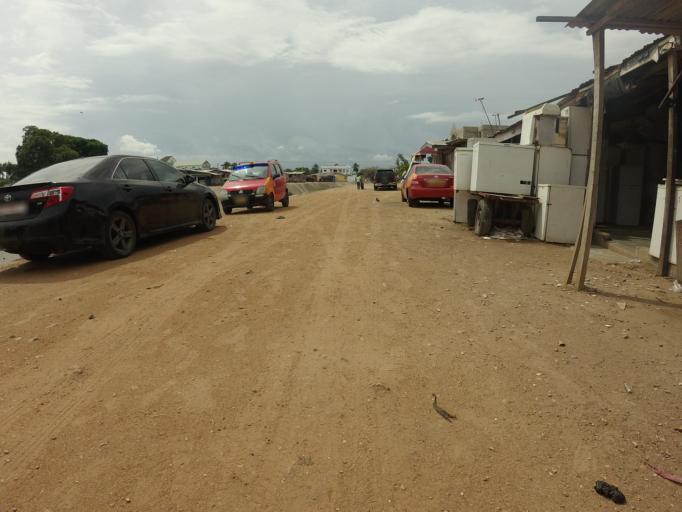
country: GH
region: Greater Accra
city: Accra
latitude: 5.5993
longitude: -0.2210
